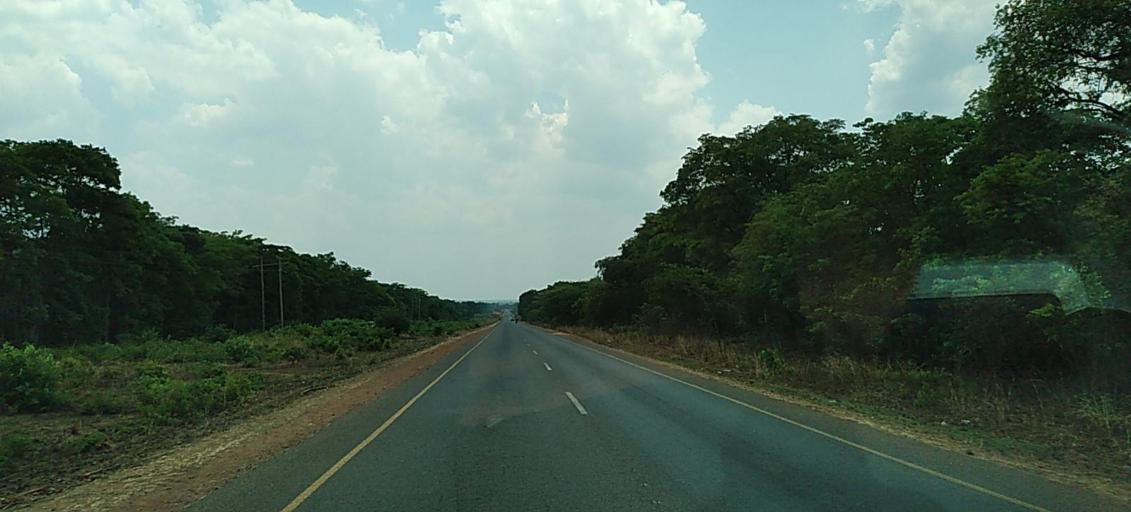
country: ZM
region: Copperbelt
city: Kalulushi
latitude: -12.8452
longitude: 28.0324
